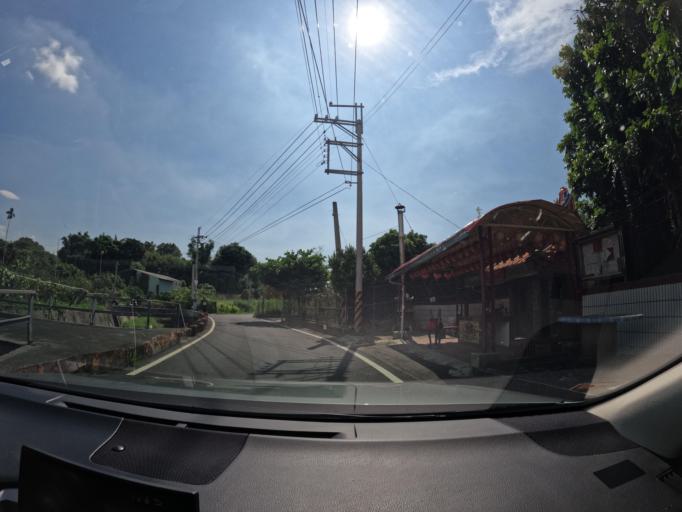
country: TW
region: Taiwan
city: Fengyuan
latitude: 24.3141
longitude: 120.7415
